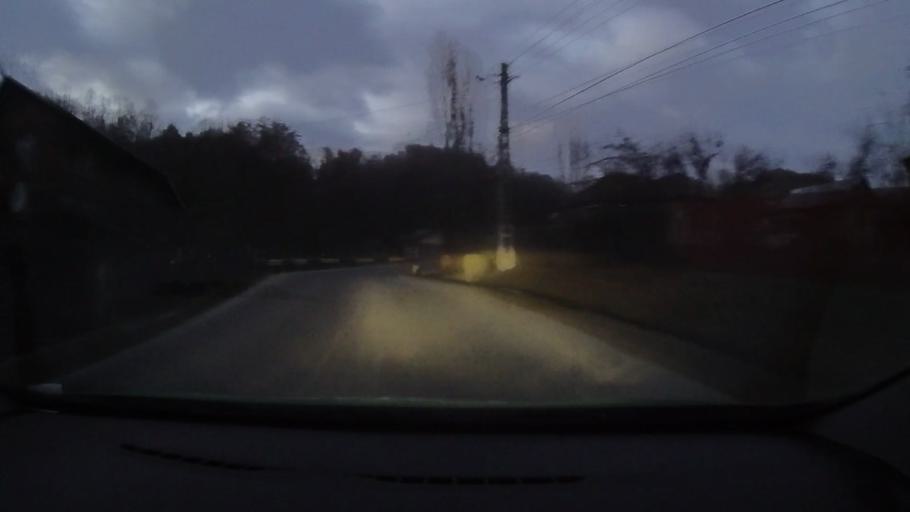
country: RO
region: Prahova
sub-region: Comuna Poiana Campina
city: Poiana Campina
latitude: 45.1272
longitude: 25.6772
